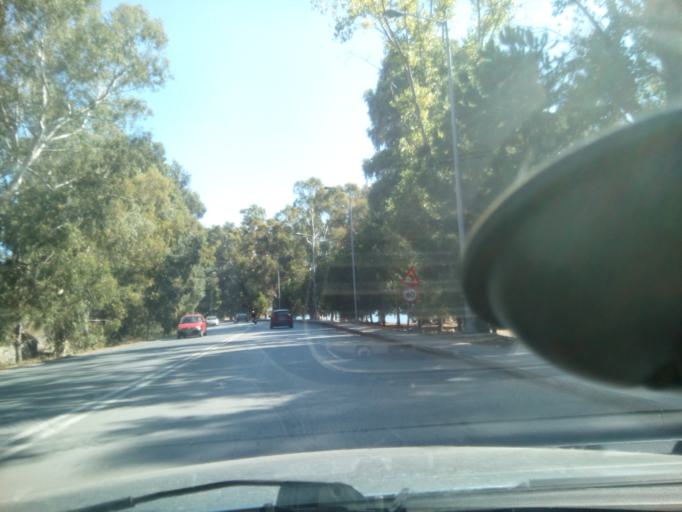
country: GR
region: Central Greece
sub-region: Nomos Evvoias
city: Chalkida
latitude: 38.4503
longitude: 23.6152
